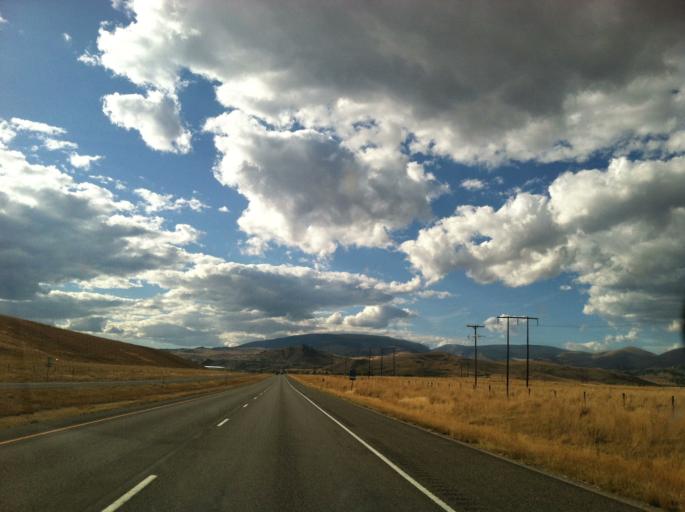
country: US
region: Montana
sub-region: Deer Lodge County
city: Anaconda
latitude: 46.1230
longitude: -112.8845
